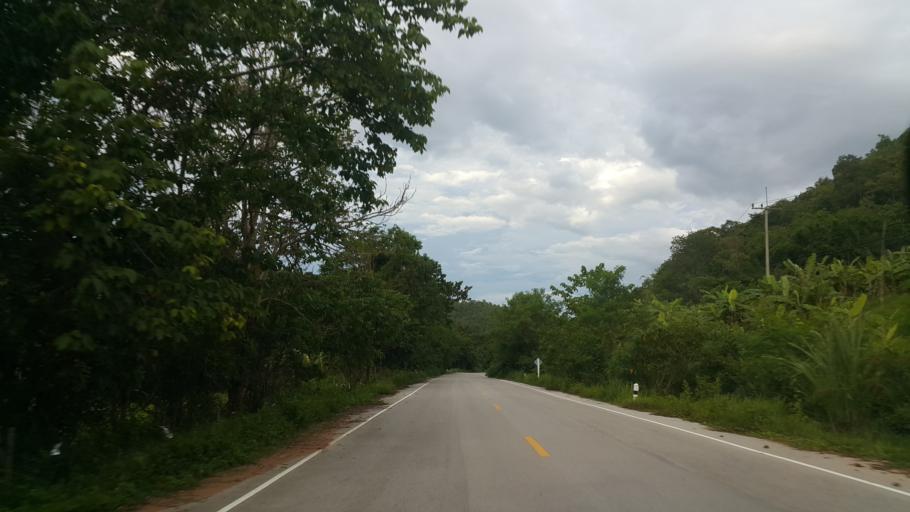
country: TH
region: Loei
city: Na Haeo
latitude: 17.4932
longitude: 101.0980
